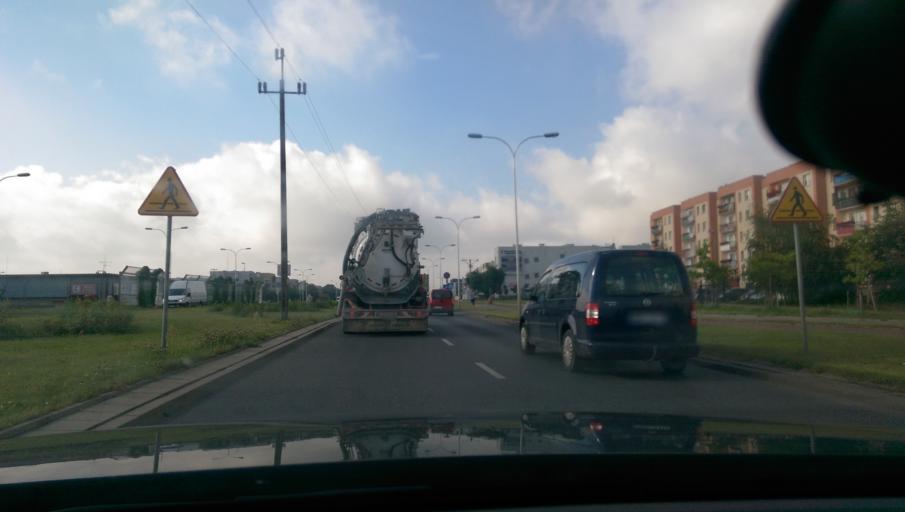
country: PL
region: Masovian Voivodeship
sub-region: Powiat ciechanowski
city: Ciechanow
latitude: 52.8784
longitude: 20.6281
